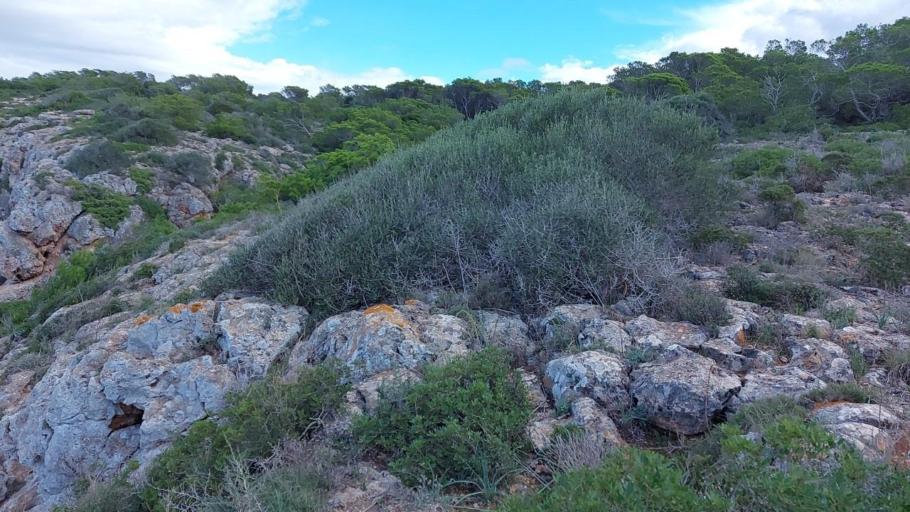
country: ES
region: Balearic Islands
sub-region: Illes Balears
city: s'Arenal
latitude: 39.4012
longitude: 2.7470
